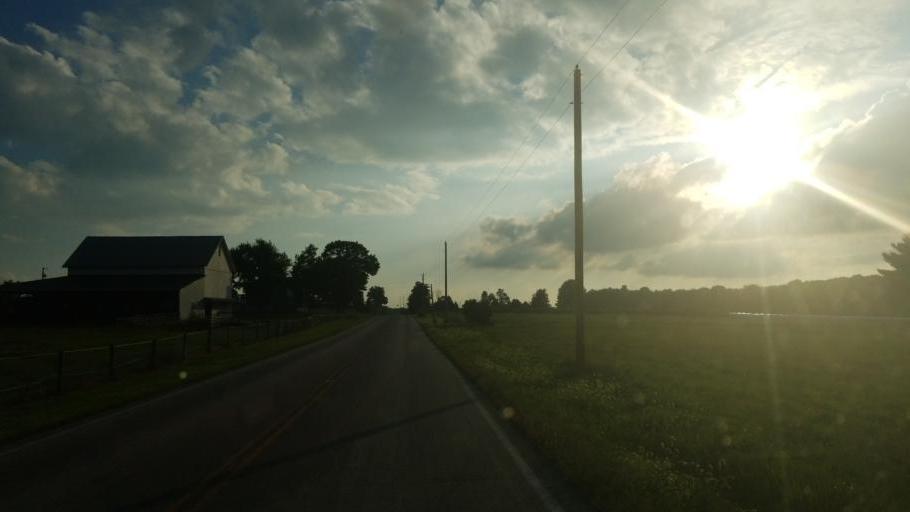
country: US
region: Ohio
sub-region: Ashland County
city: Loudonville
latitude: 40.7411
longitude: -82.1664
